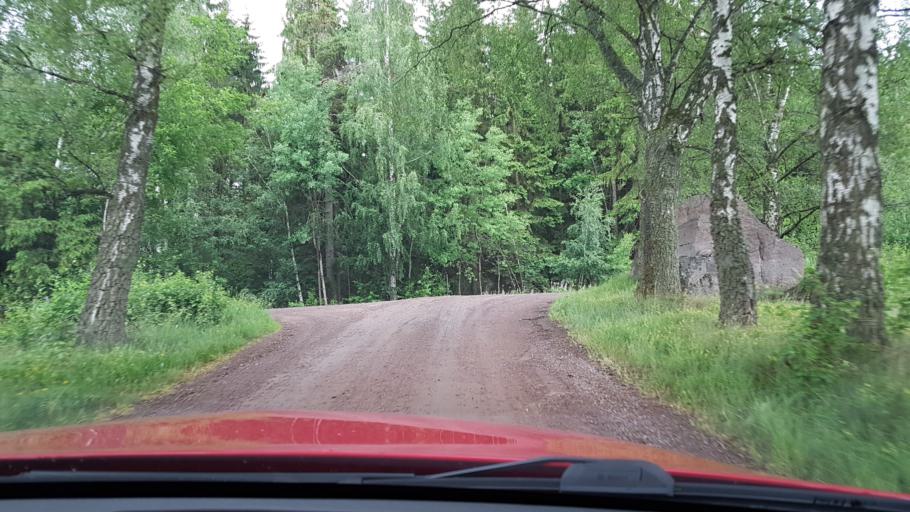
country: SE
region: Vaestra Goetaland
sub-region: Tibro Kommun
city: Tibro
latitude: 58.4289
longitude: 14.1254
